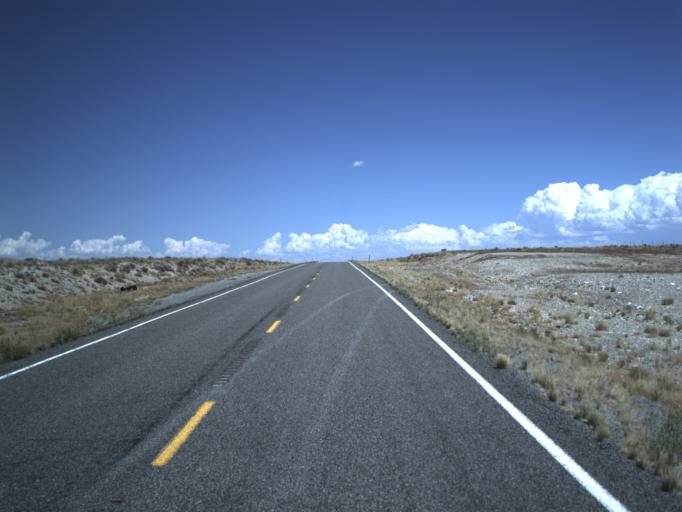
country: US
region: Utah
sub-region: Millard County
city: Delta
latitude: 39.1490
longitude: -113.0713
